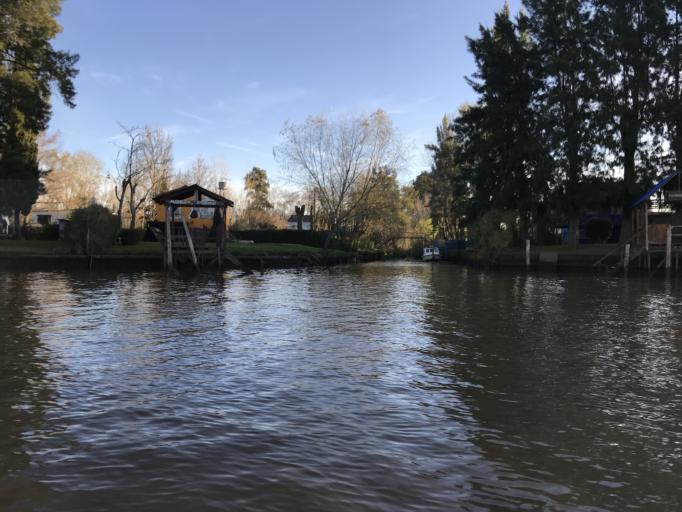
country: AR
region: Buenos Aires
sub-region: Partido de Tigre
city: Tigre
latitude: -34.3880
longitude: -58.5779
